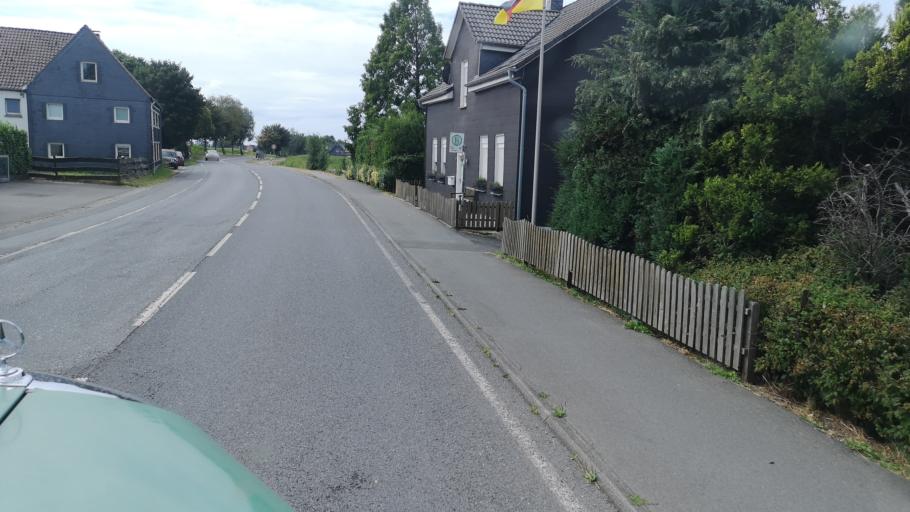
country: DE
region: North Rhine-Westphalia
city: Radevormwald
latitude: 51.1787
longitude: 7.3633
